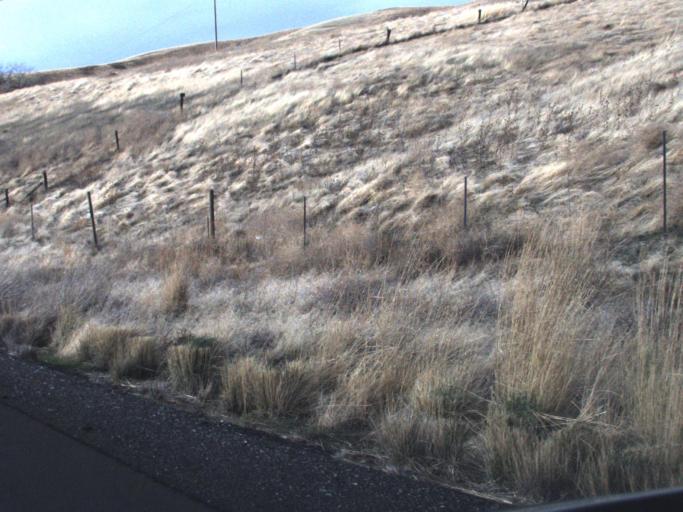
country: US
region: Washington
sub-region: Garfield County
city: Pomeroy
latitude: 46.4627
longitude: -117.6898
